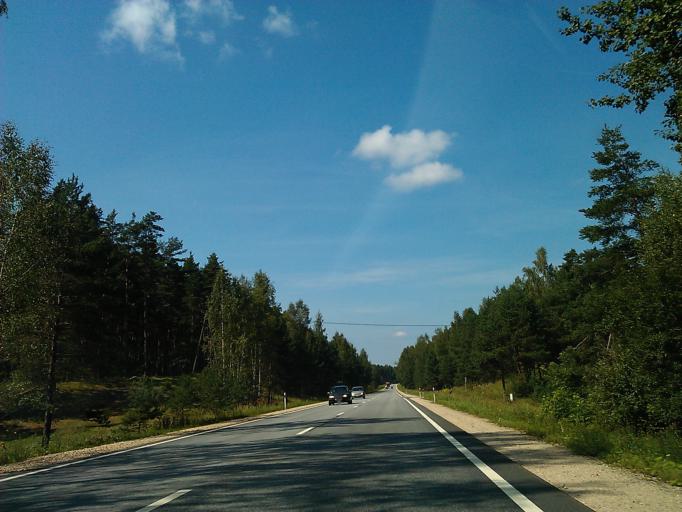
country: LV
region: Riga
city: Bergi
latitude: 56.9670
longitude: 24.3606
